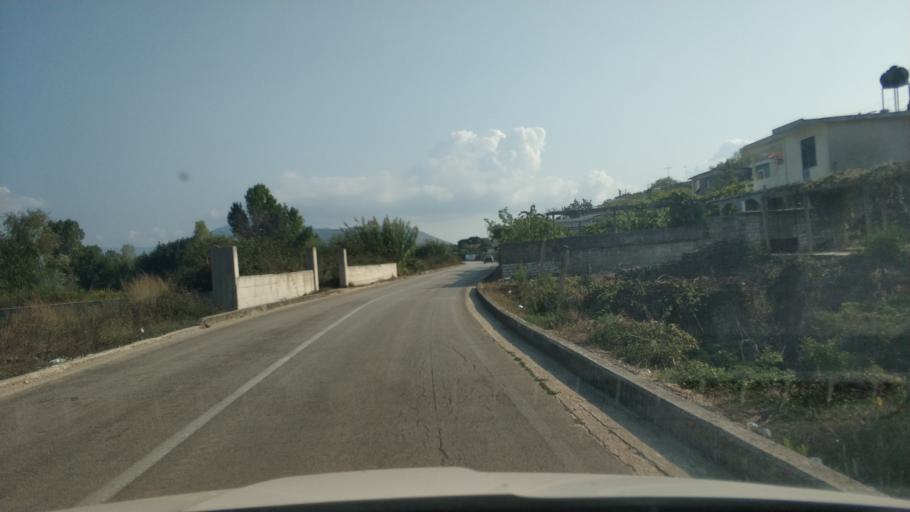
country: AL
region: Vlore
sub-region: Rrethi i Sarandes
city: Sarande
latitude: 39.8456
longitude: 20.0368
